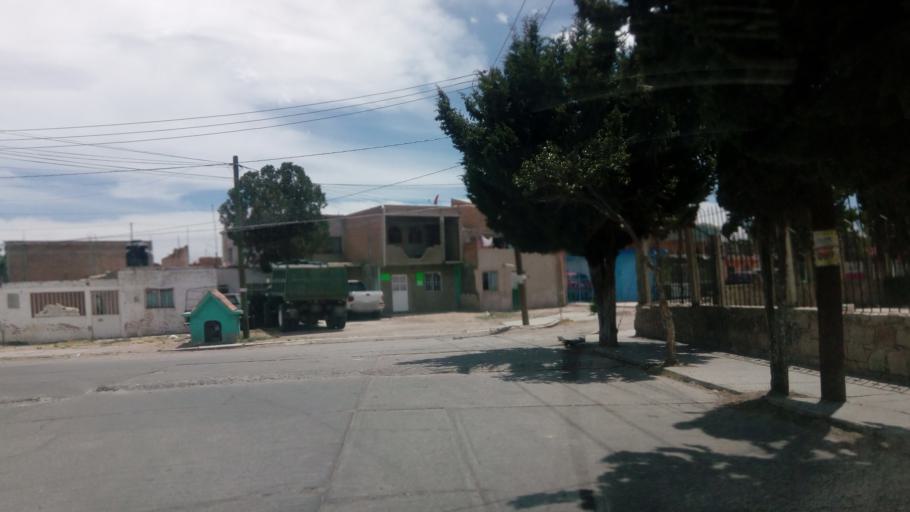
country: MX
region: Durango
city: Victoria de Durango
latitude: 24.0032
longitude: -104.6780
